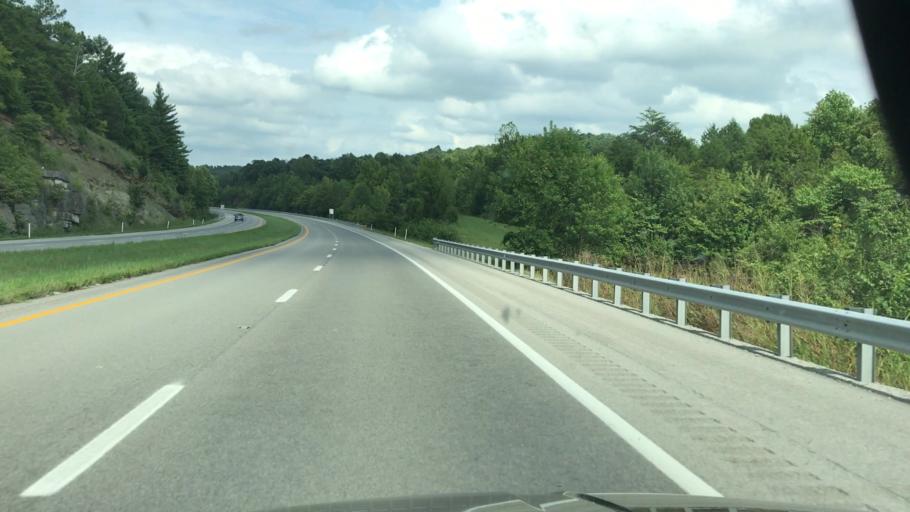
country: US
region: Kentucky
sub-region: Hopkins County
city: Dawson Springs
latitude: 37.1563
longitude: -87.7708
